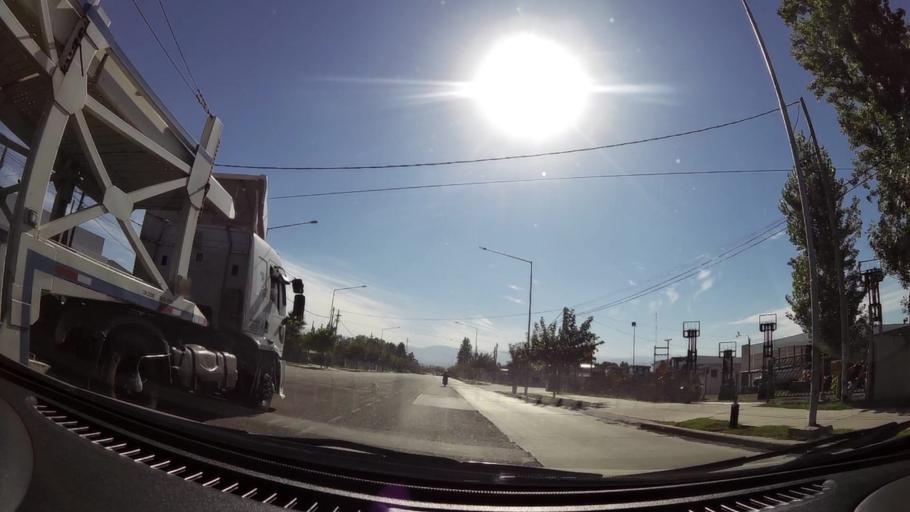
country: AR
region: Mendoza
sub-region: Departamento de Godoy Cruz
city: Godoy Cruz
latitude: -32.9316
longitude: -68.8003
